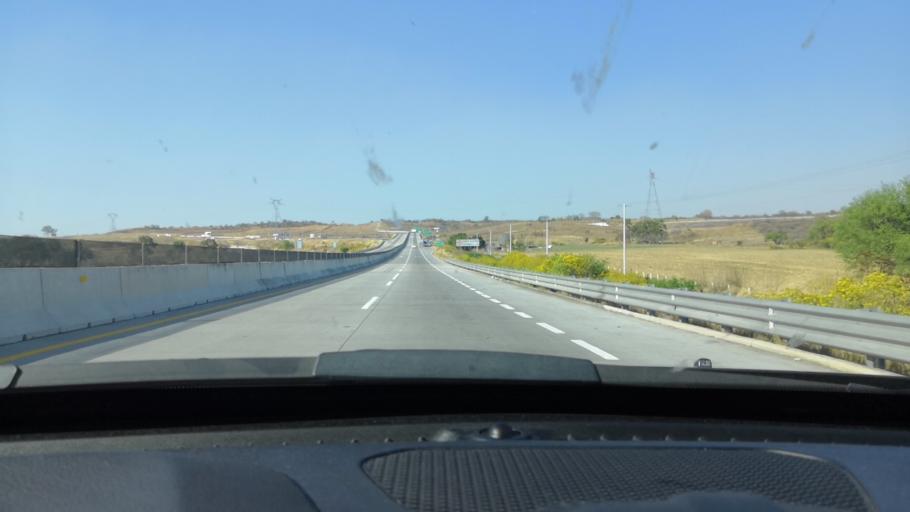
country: MX
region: Jalisco
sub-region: Zapotlanejo
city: La Mezquitera
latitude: 20.5785
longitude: -103.1004
